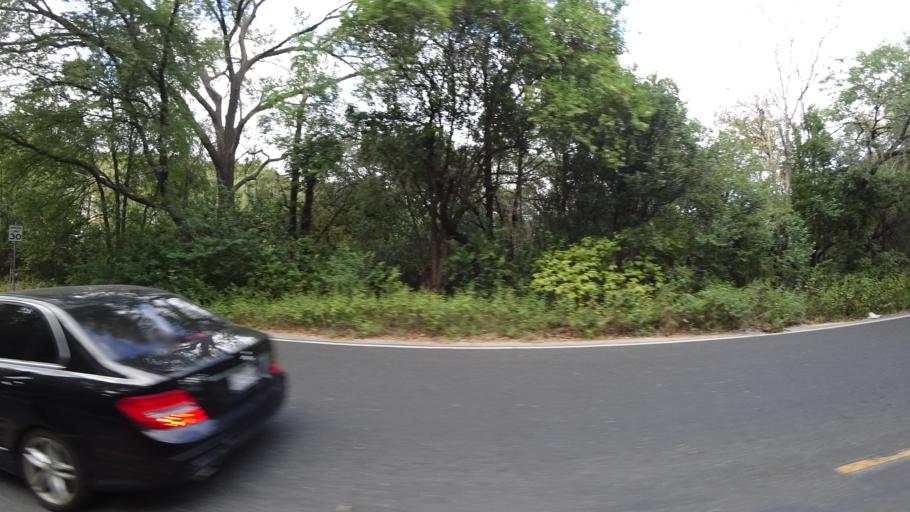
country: US
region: Texas
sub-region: Travis County
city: West Lake Hills
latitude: 30.2916
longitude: -97.7976
